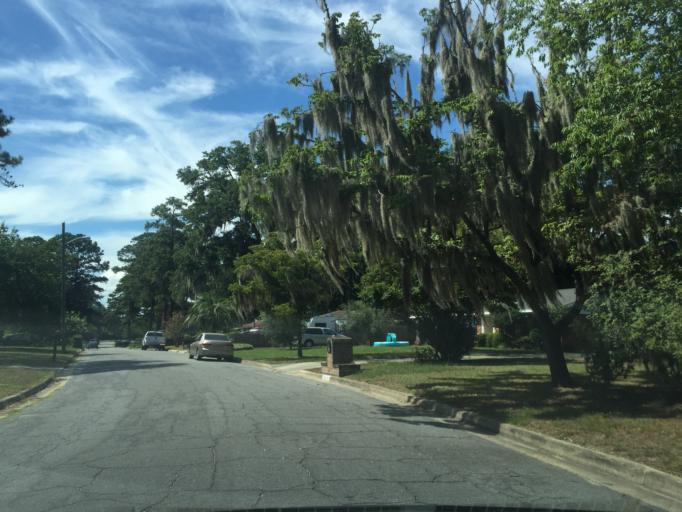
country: US
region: Georgia
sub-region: Chatham County
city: Montgomery
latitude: 31.9782
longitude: -81.1098
